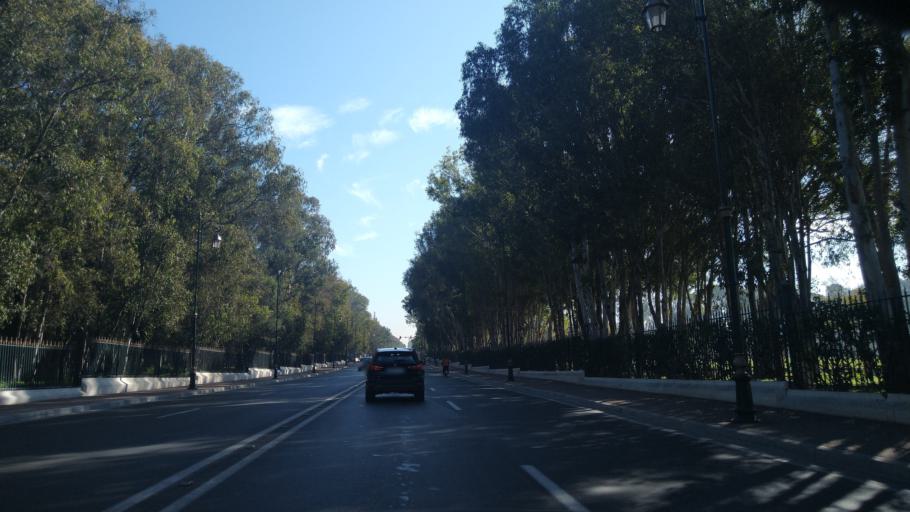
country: MA
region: Rabat-Sale-Zemmour-Zaer
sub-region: Rabat
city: Rabat
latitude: 33.9833
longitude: -6.8471
